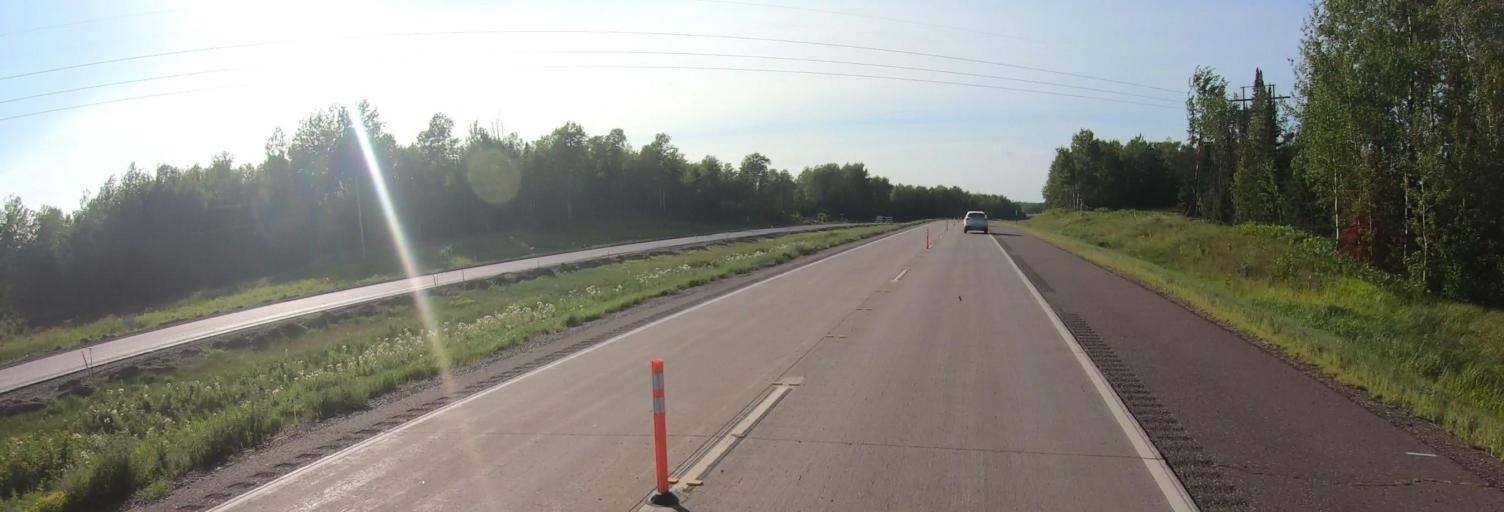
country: US
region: Minnesota
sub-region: Saint Louis County
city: Hermantown
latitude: 46.9146
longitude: -92.3954
